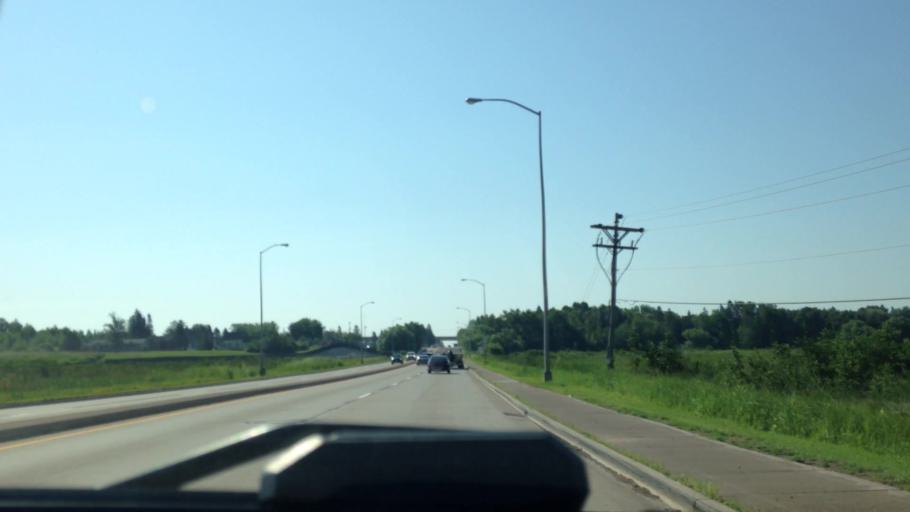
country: US
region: Wisconsin
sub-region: Douglas County
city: Superior
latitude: 46.6957
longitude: -92.0332
